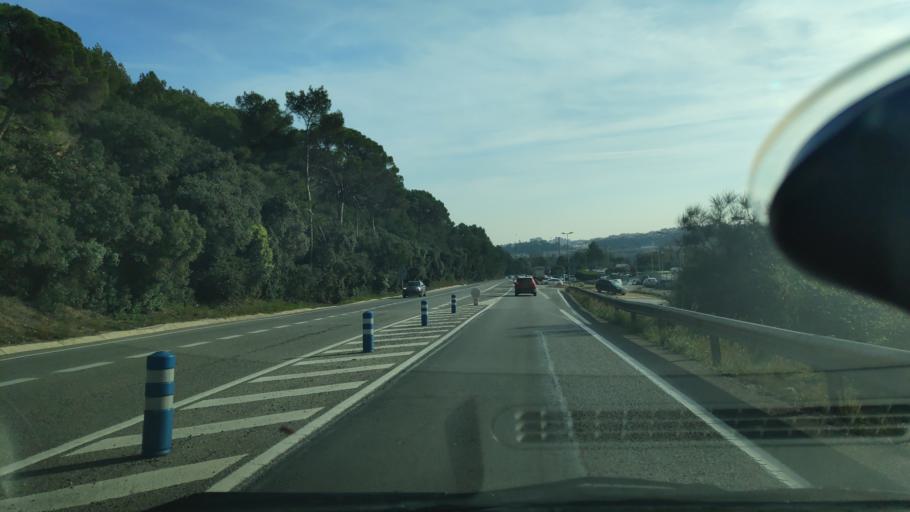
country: ES
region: Catalonia
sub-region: Provincia de Barcelona
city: Castellar del Valles
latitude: 41.5807
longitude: 2.0907
